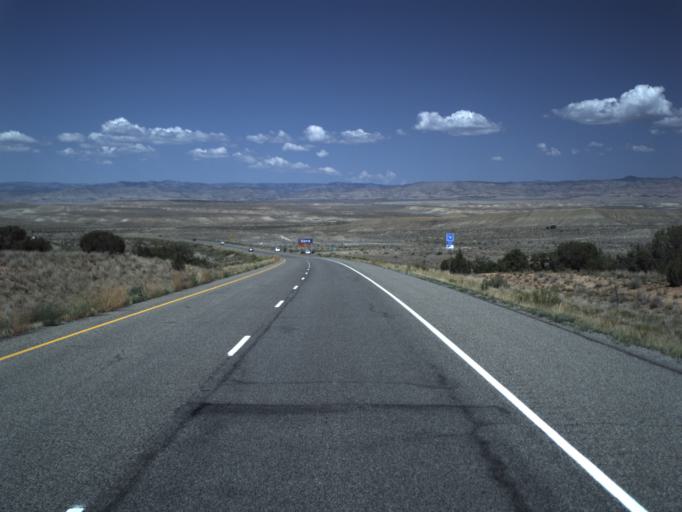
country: US
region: Colorado
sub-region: Mesa County
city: Loma
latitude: 39.1933
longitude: -109.0486
